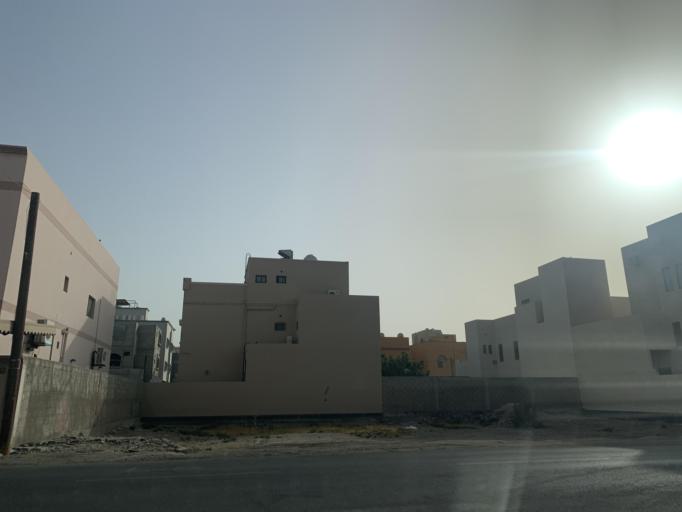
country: BH
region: Central Governorate
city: Madinat Hamad
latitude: 26.1560
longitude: 50.5101
